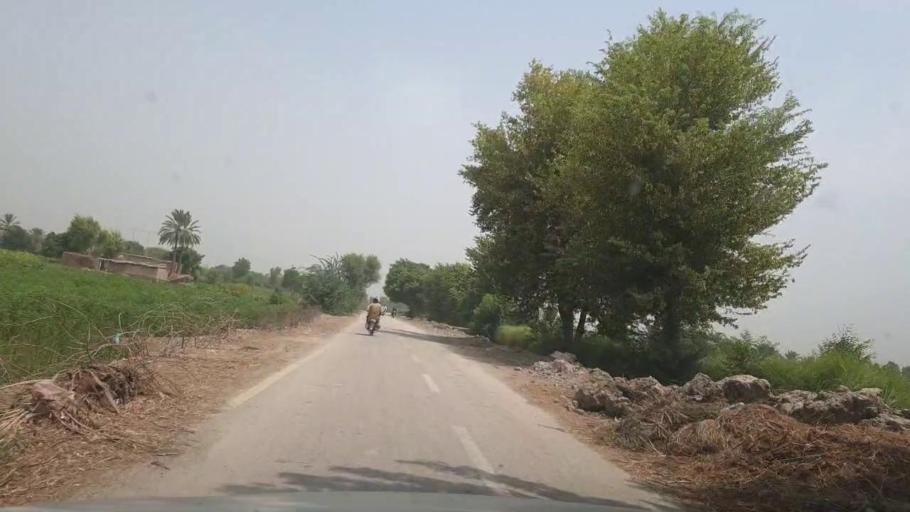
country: PK
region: Sindh
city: Kot Diji
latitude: 27.3827
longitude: 68.6546
